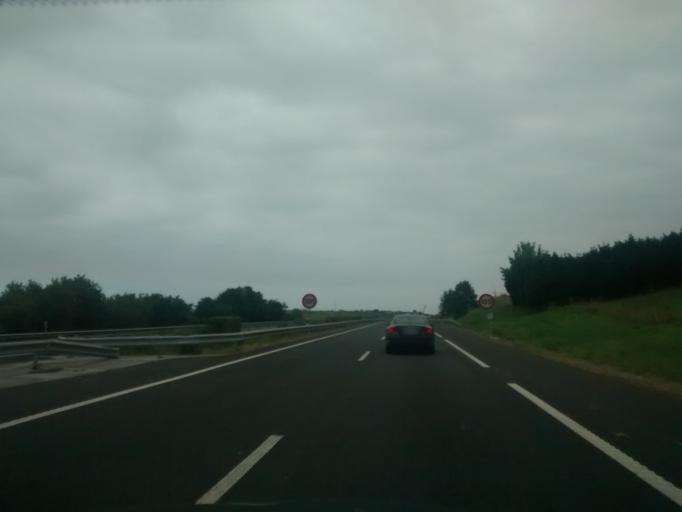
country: ES
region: Cantabria
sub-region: Provincia de Cantabria
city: Santa Cruz de Bezana
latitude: 43.4458
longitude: -3.8871
